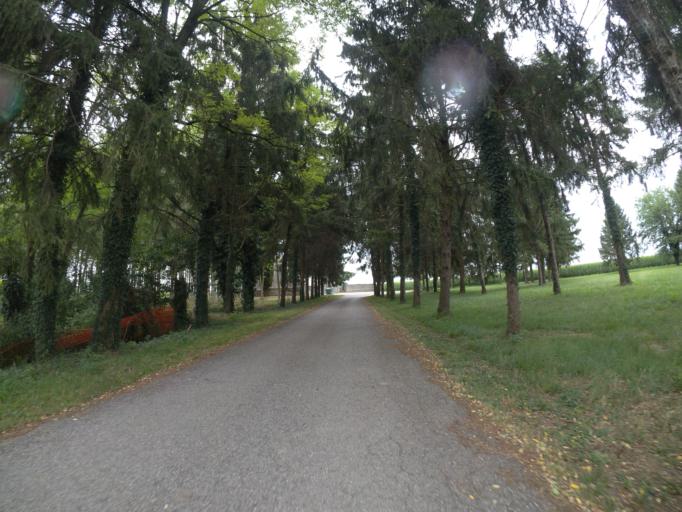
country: IT
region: Friuli Venezia Giulia
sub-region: Provincia di Udine
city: Varmo
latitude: 45.8701
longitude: 13.0056
